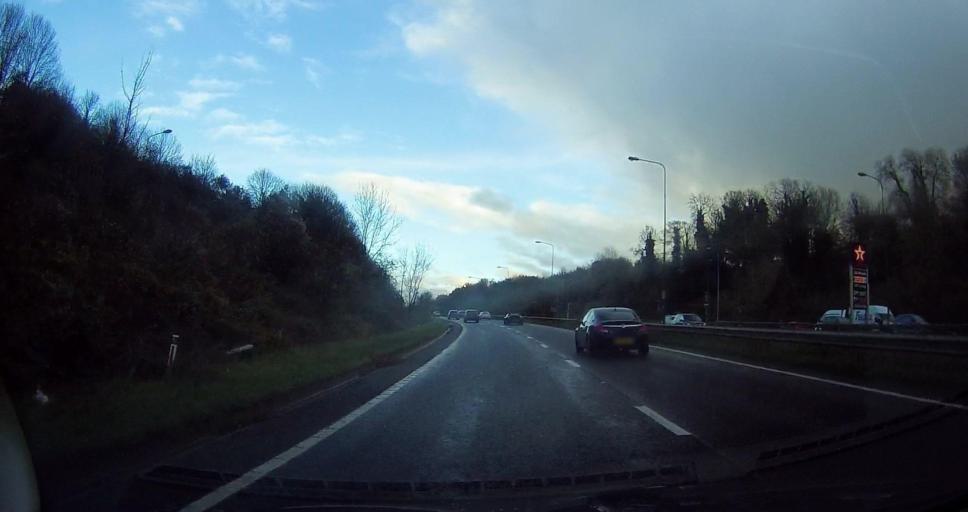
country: GB
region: England
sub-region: West Sussex
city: Hassocks
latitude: 50.9020
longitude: -0.1801
